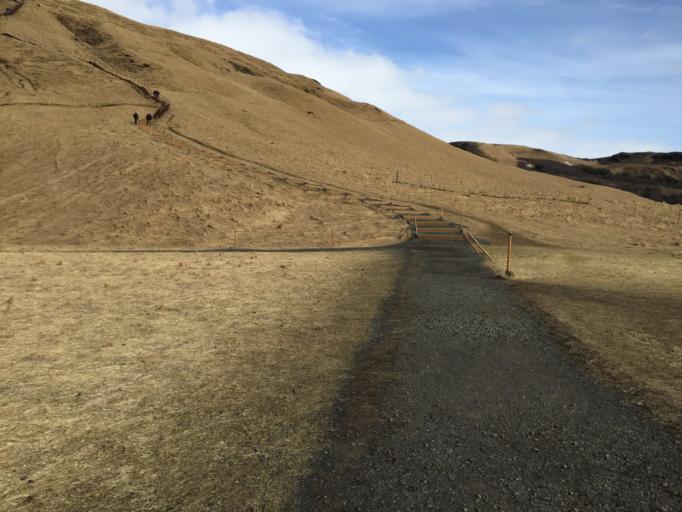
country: IS
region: South
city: Vestmannaeyjar
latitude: 63.5301
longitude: -19.5121
